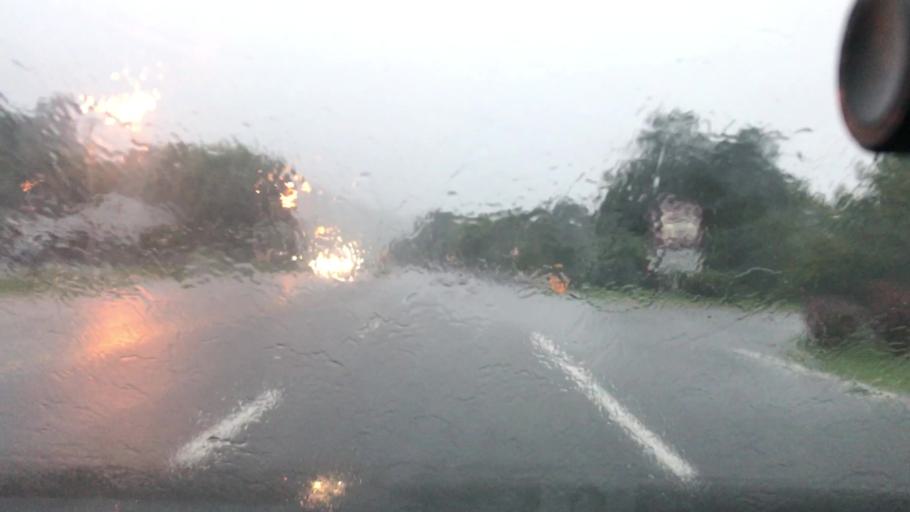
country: US
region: Virginia
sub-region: Giles County
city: Narrows
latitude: 37.3370
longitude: -80.7975
